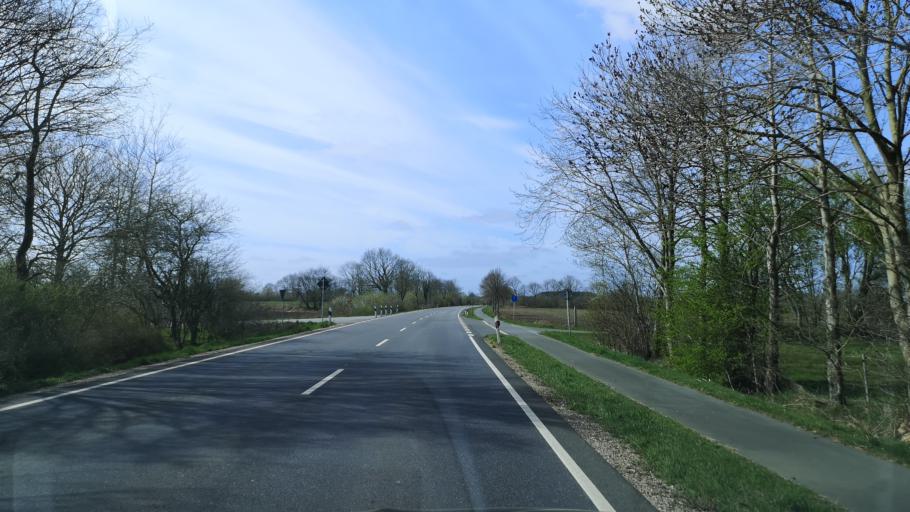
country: DE
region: Schleswig-Holstein
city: Wrohm
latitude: 54.2179
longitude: 9.4041
